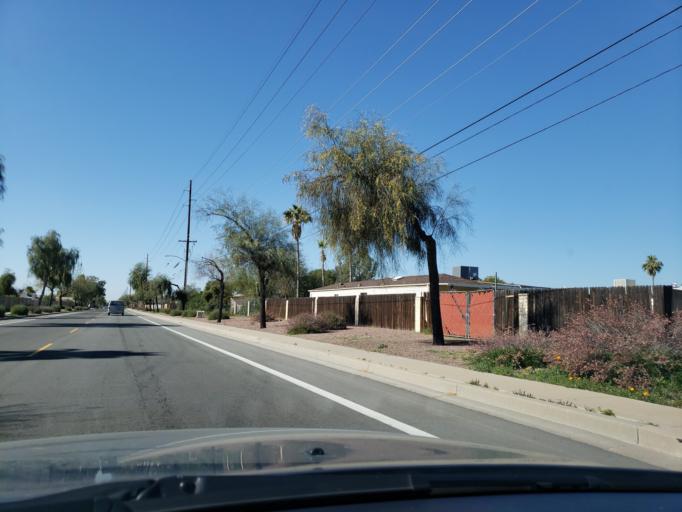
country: US
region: Arizona
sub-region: Maricopa County
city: Glendale
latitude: 33.6475
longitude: -112.0691
